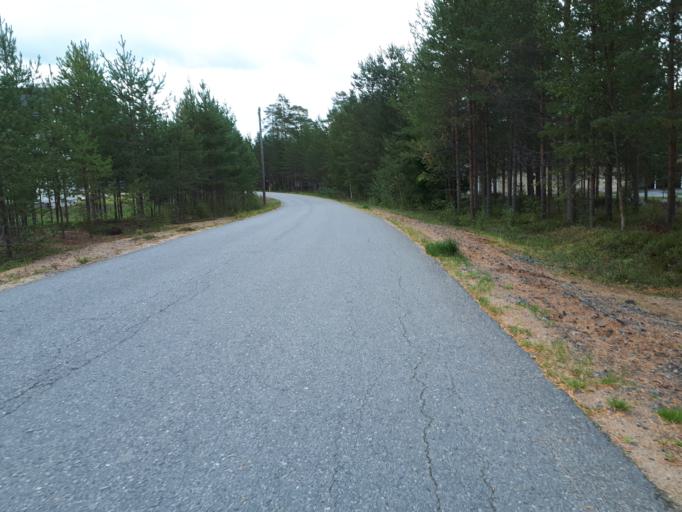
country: FI
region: Northern Ostrobothnia
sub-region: Oulunkaari
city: Ii
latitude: 65.3241
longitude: 25.3994
